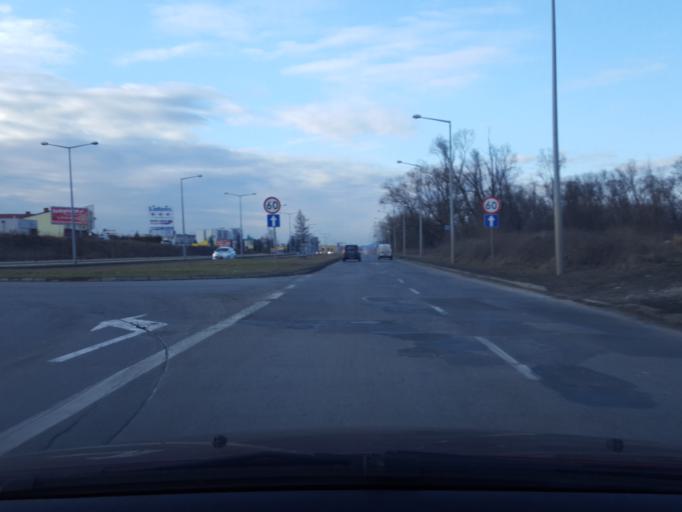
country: PL
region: Lesser Poland Voivodeship
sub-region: Powiat nowosadecki
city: Nawojowa
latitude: 49.5950
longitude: 20.7324
